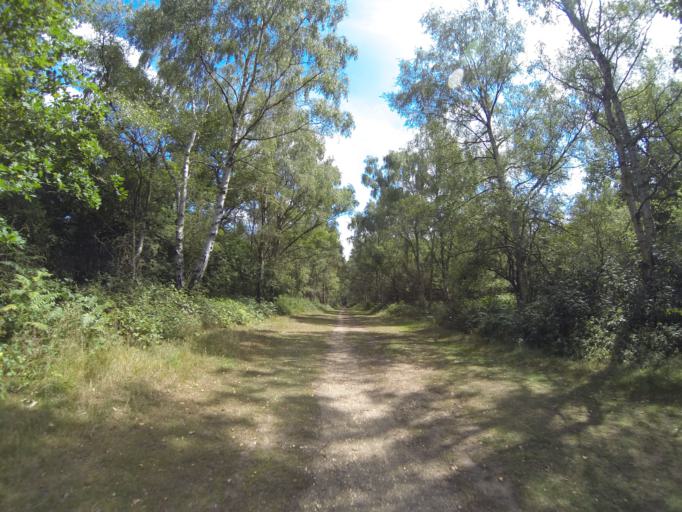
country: GB
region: England
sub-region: Greater London
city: Bexley
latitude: 51.4395
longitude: 0.1789
